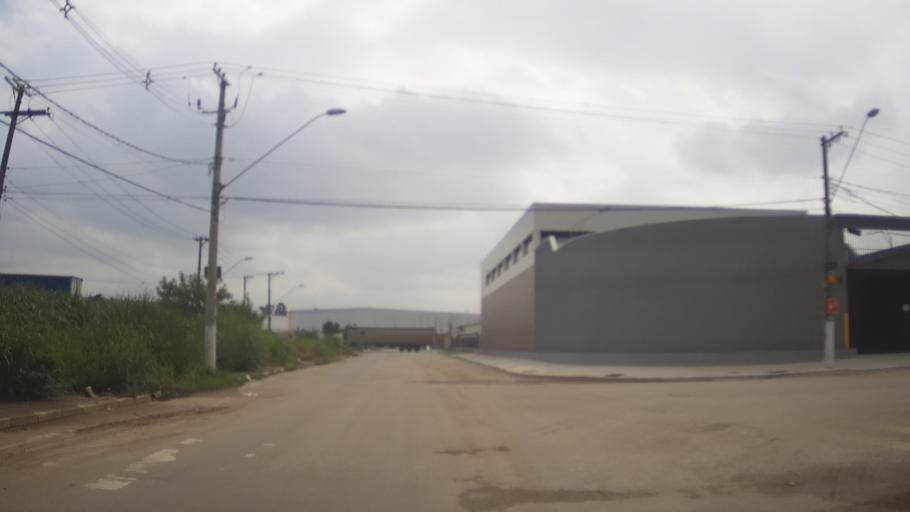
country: BR
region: Sao Paulo
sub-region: Guarulhos
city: Guarulhos
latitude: -23.4685
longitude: -46.4770
